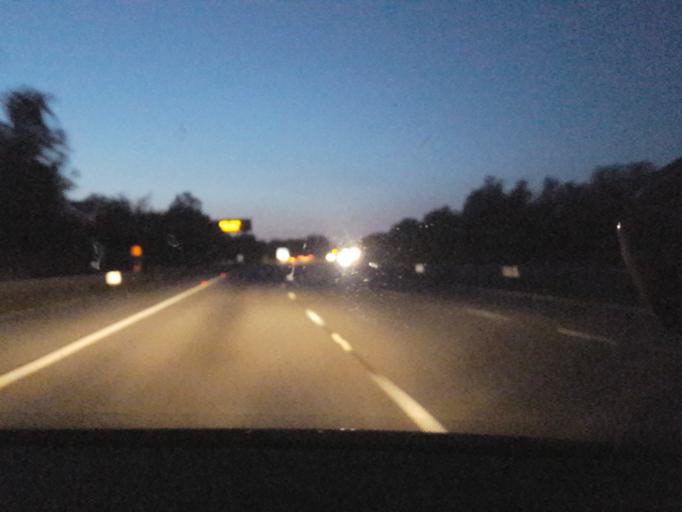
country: GB
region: England
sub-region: Leicestershire
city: Markfield
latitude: 52.6800
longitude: -1.2885
